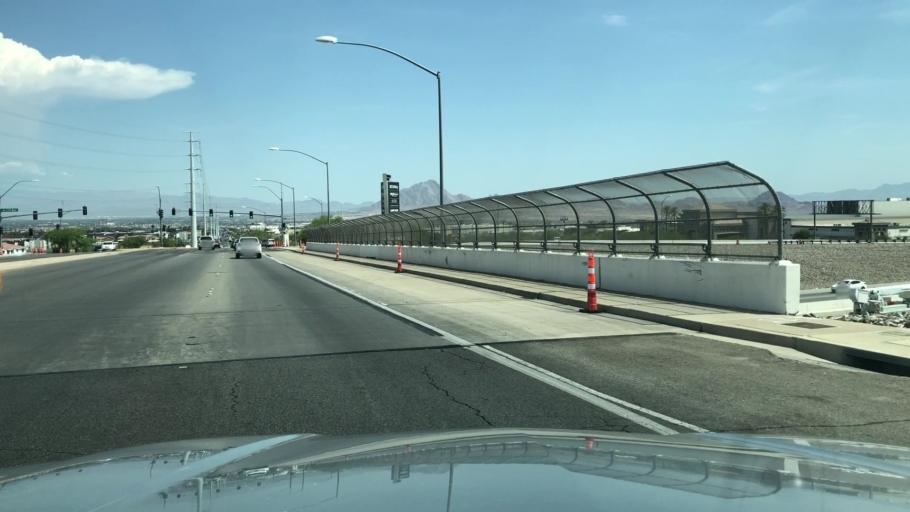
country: US
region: Nevada
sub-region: Clark County
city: Whitney
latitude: 36.0289
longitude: -115.0470
